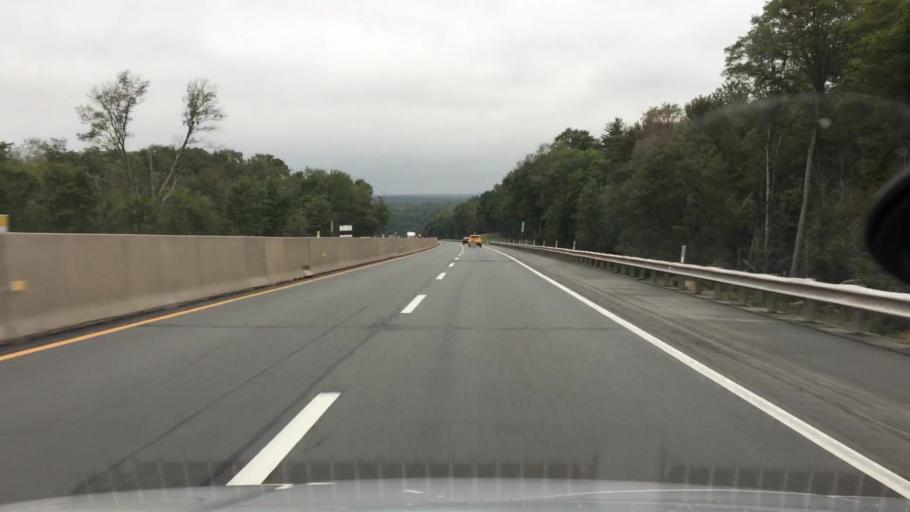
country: US
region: Pennsylvania
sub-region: Luzerne County
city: White Haven
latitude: 41.0940
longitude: -75.7417
